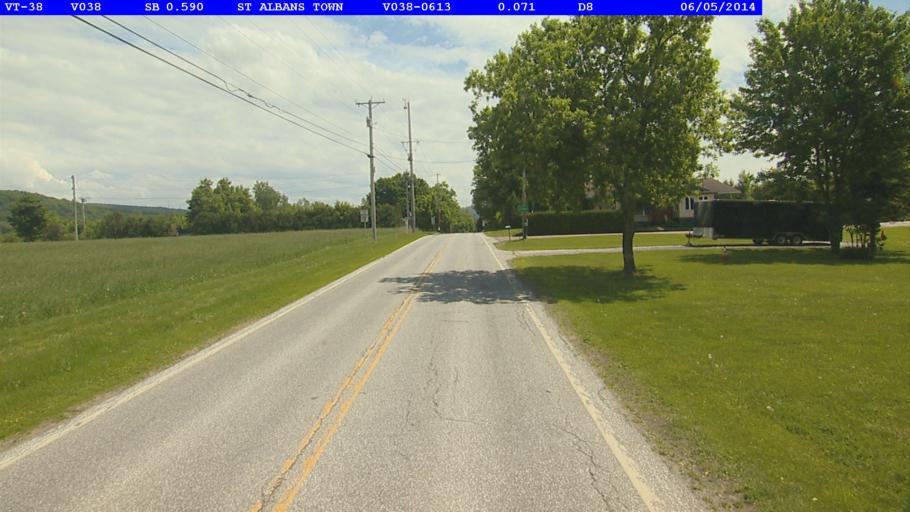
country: US
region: Vermont
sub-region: Franklin County
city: Saint Albans
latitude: 44.8249
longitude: -73.0897
